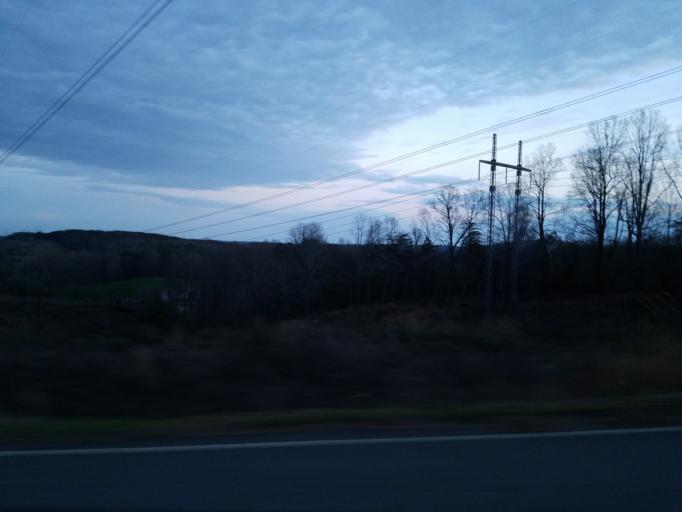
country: US
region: Georgia
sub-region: Cherokee County
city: Ball Ground
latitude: 34.3224
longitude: -84.3847
